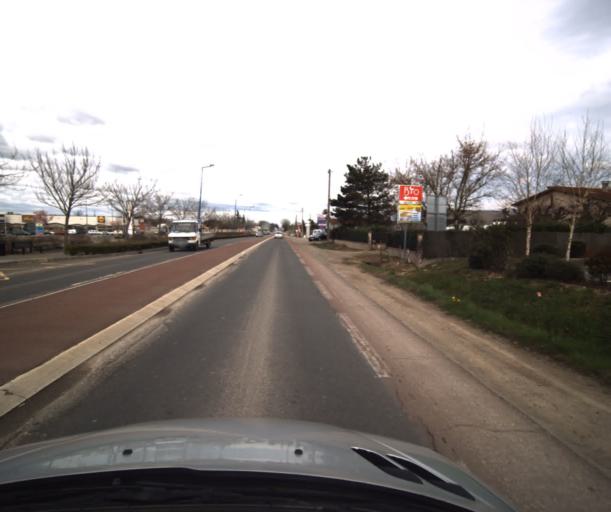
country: FR
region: Midi-Pyrenees
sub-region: Departement du Tarn-et-Garonne
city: Montauban
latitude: 44.0407
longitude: 1.3846
